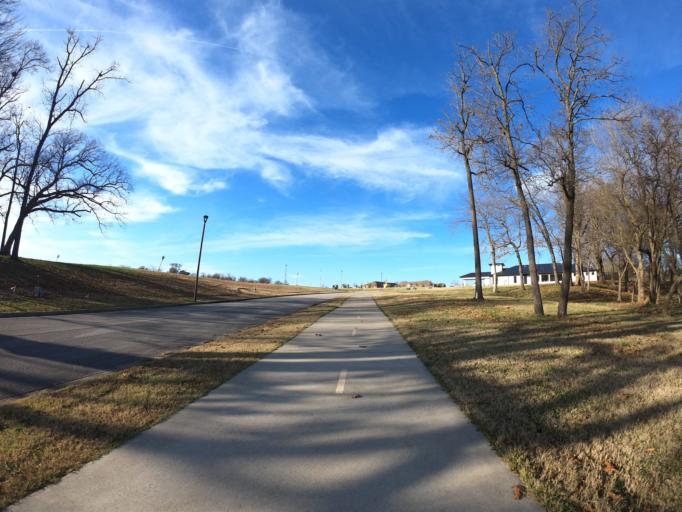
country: US
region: Arkansas
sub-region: Benton County
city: Rogers
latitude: 36.3230
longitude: -94.1758
